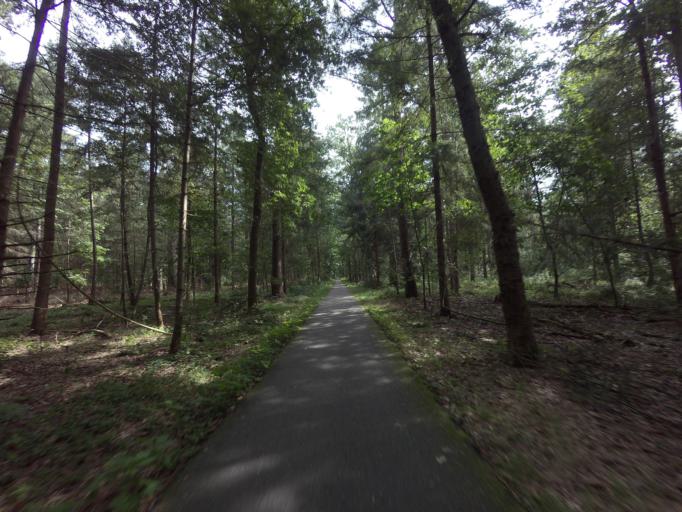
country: NL
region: Drenthe
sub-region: Gemeente Borger-Odoorn
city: Borger
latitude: 52.8660
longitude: 6.7235
